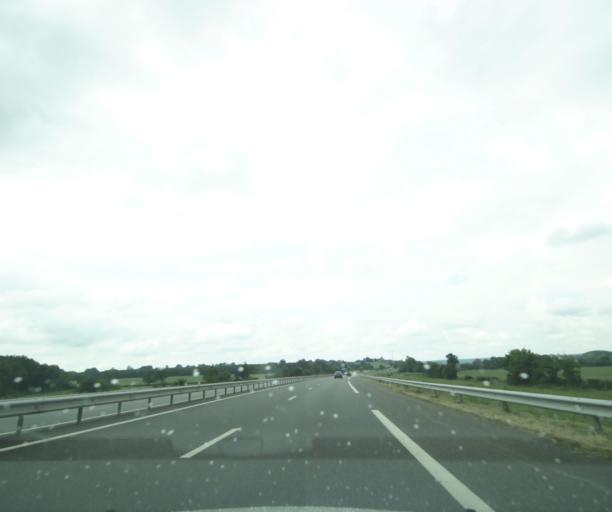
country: FR
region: Centre
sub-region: Departement du Cher
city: Orval
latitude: 46.6848
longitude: 2.4584
